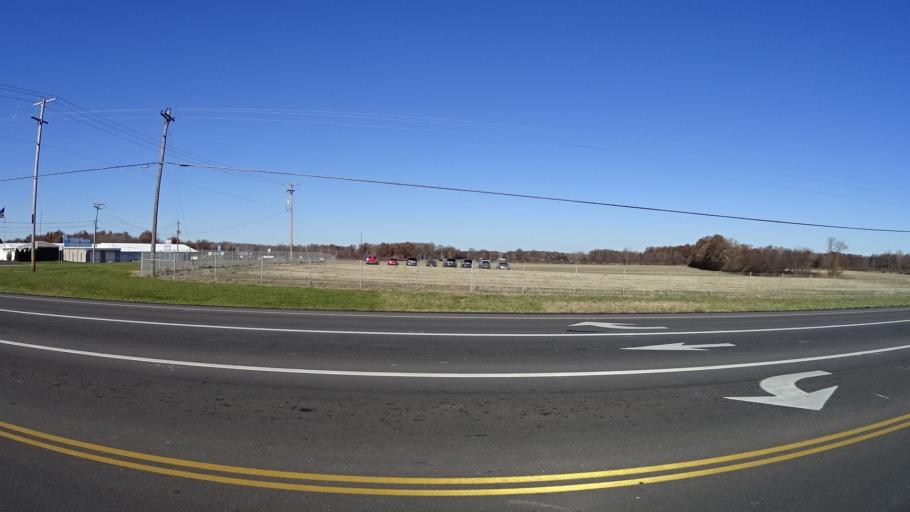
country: US
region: Ohio
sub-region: Lorain County
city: Elyria
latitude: 41.3747
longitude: -82.1618
